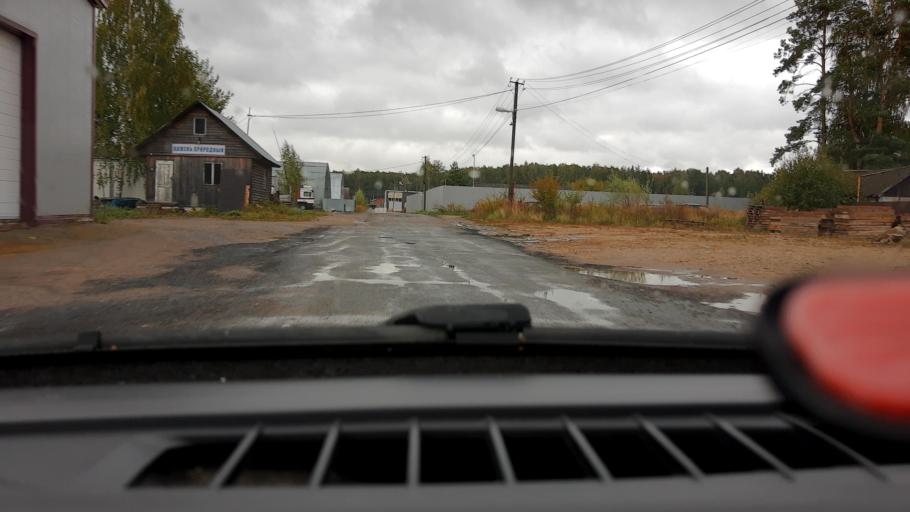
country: RU
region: Nizjnij Novgorod
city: Afonino
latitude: 56.1877
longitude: 44.1198
